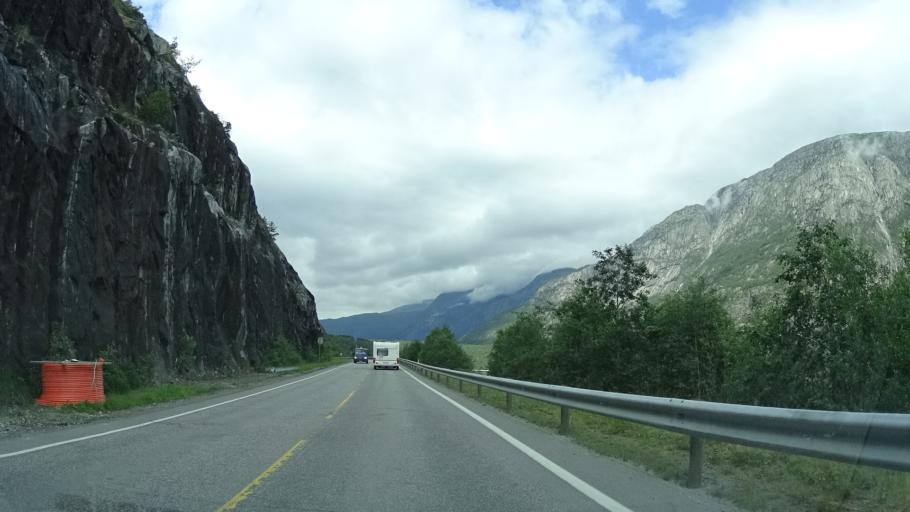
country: NO
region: Hordaland
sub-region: Eidfjord
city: Eidfjord
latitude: 60.4438
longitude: 7.1066
